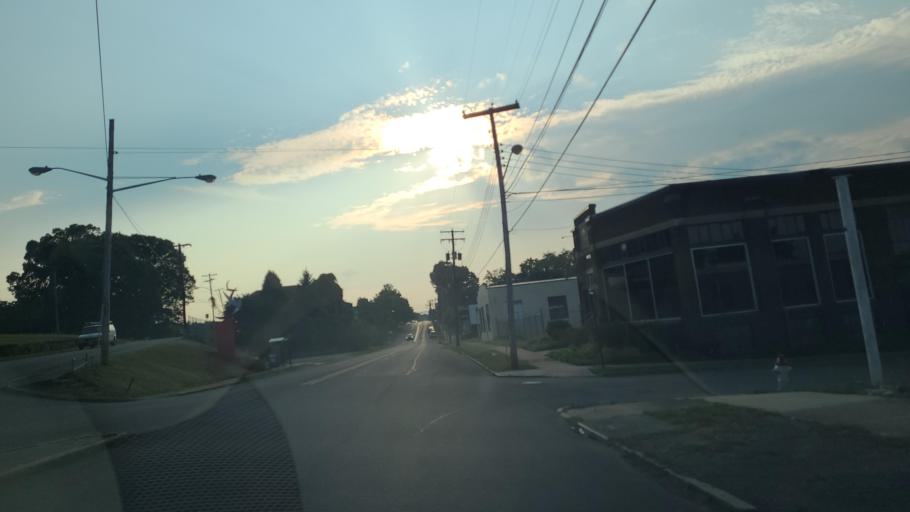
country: US
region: Virginia
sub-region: City of Roanoke
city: Roanoke
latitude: 37.2712
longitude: -79.9542
